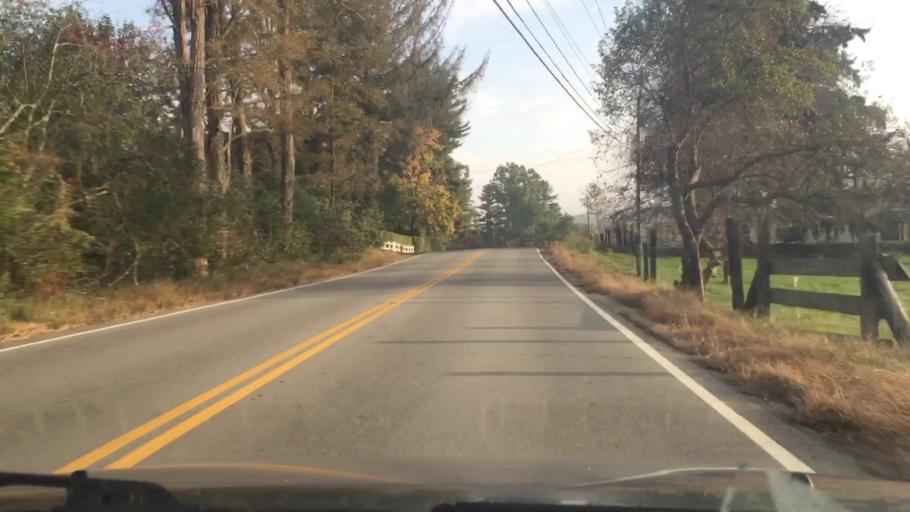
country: US
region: New Hampshire
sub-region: Cheshire County
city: Swanzey
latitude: 42.8500
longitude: -72.2787
